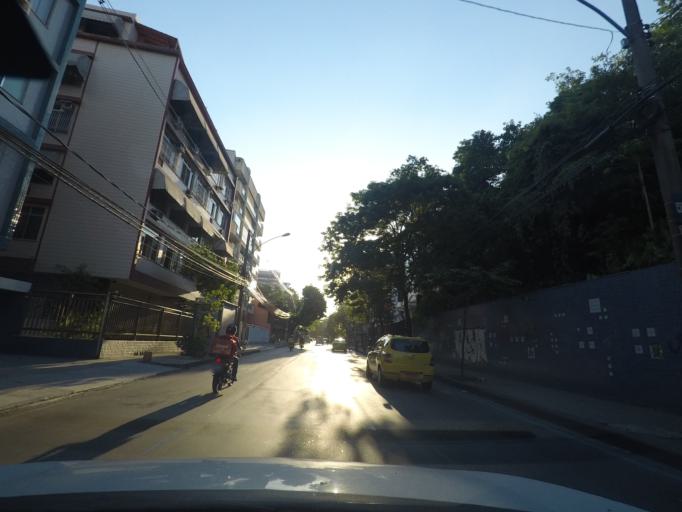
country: BR
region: Rio de Janeiro
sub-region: Rio De Janeiro
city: Rio de Janeiro
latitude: -22.9169
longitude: -43.2139
